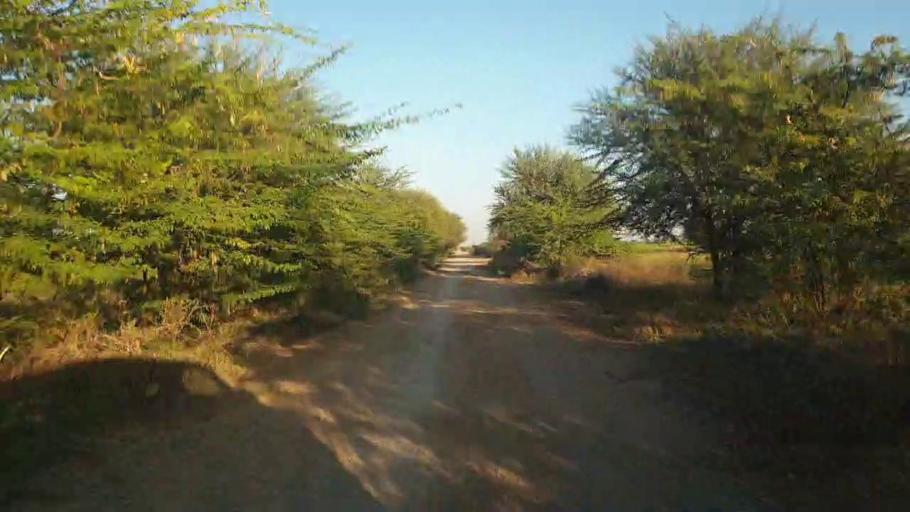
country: PK
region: Sindh
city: Dhoro Naro
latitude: 25.3599
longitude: 69.5667
